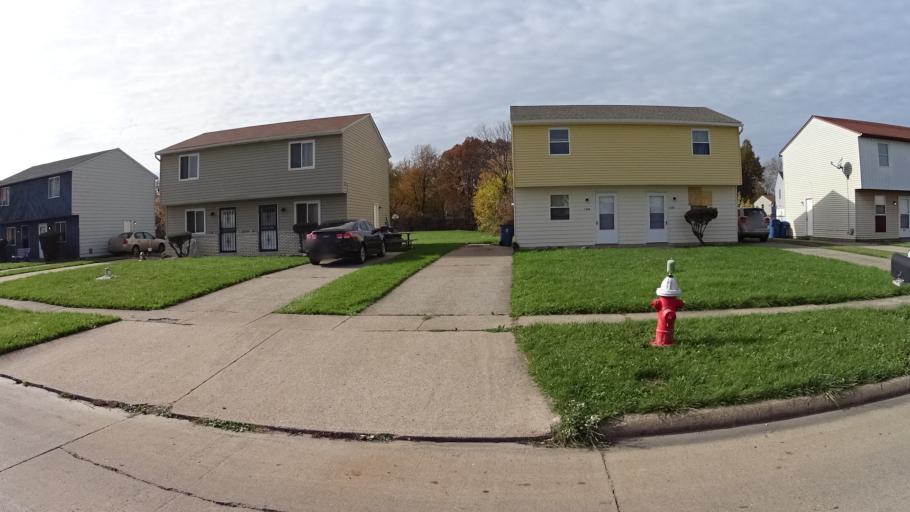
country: US
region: Ohio
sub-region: Lorain County
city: Lorain
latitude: 41.4700
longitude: -82.1516
